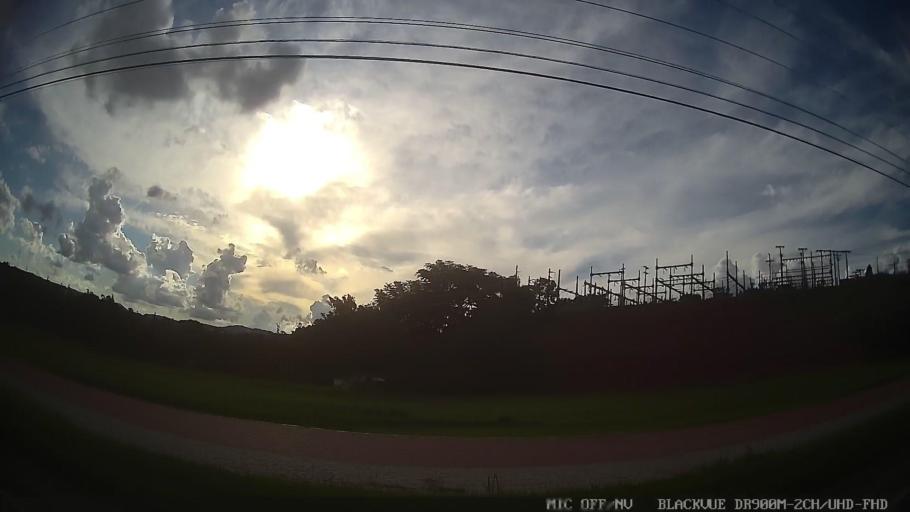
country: BR
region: Minas Gerais
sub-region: Extrema
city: Extrema
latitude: -22.8598
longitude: -46.3301
